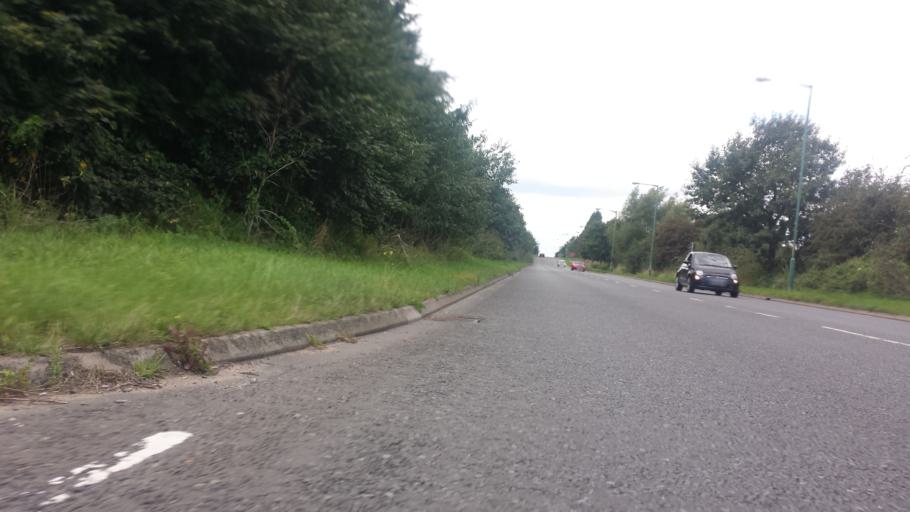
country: GB
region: England
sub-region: Kent
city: Swanley
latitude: 51.4065
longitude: 0.1548
